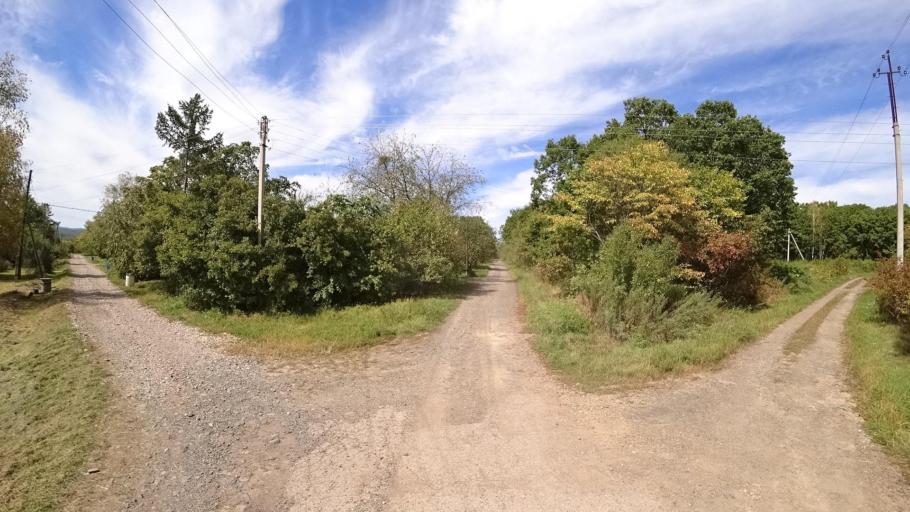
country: RU
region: Primorskiy
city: Yakovlevka
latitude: 44.6482
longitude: 133.5918
